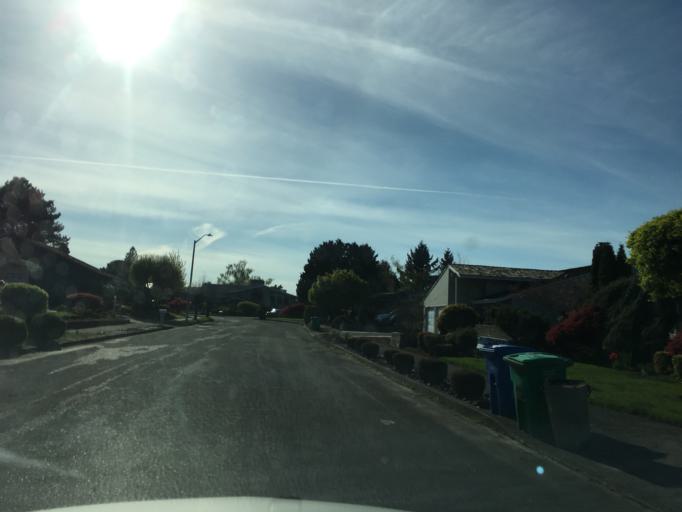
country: US
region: Oregon
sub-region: Multnomah County
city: Fairview
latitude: 45.5490
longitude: -122.5145
